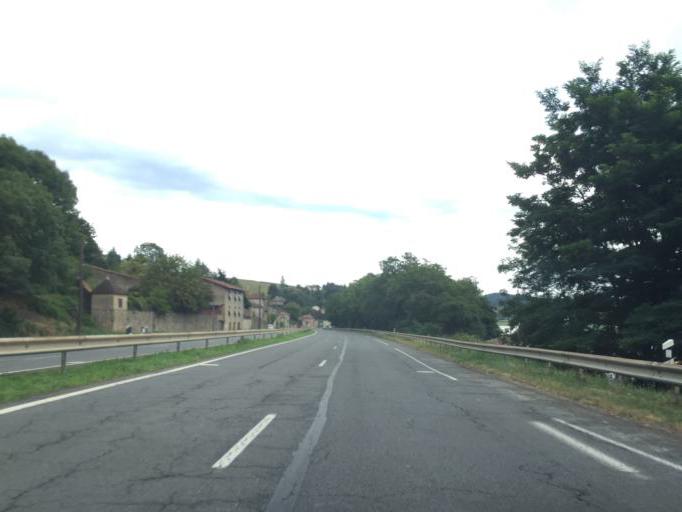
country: FR
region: Rhone-Alpes
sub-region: Departement du Rhone
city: Pontcharra-sur-Turdine
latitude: 45.8861
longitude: 4.4650
